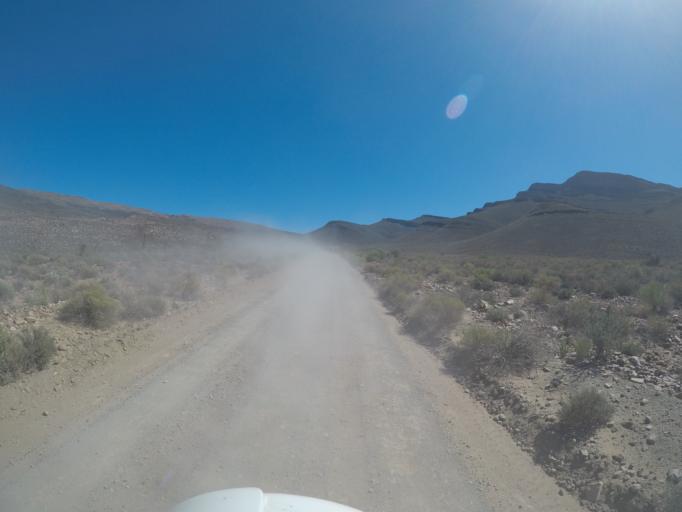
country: ZA
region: Western Cape
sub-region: West Coast District Municipality
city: Clanwilliam
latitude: -32.6347
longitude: 19.3991
